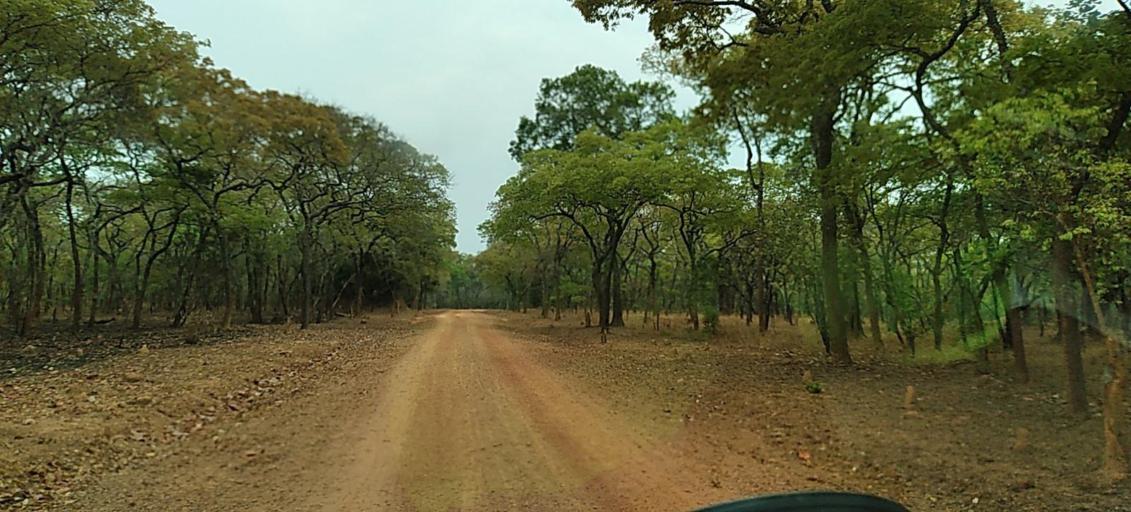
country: ZM
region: North-Western
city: Solwezi
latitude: -12.9218
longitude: 26.5608
